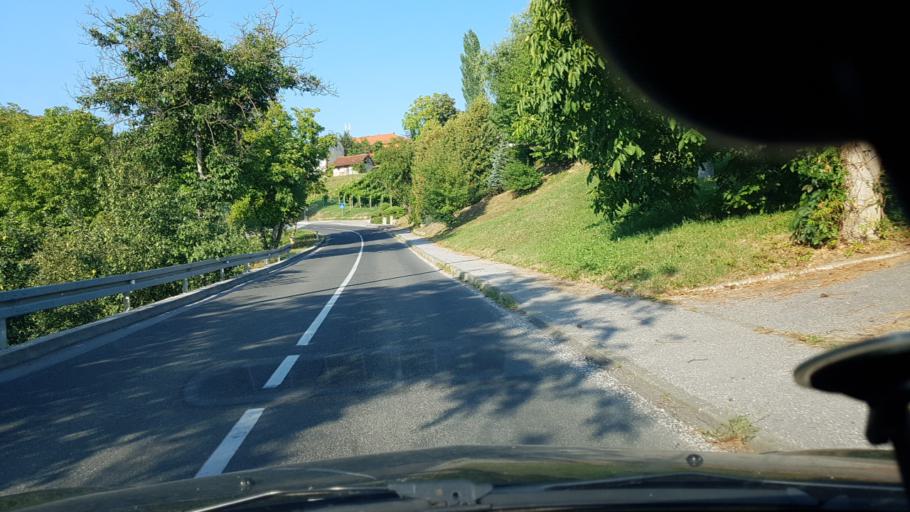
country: SI
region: Bistrica ob Sotli
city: Bistrica ob Sotli
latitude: 46.0470
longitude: 15.7366
